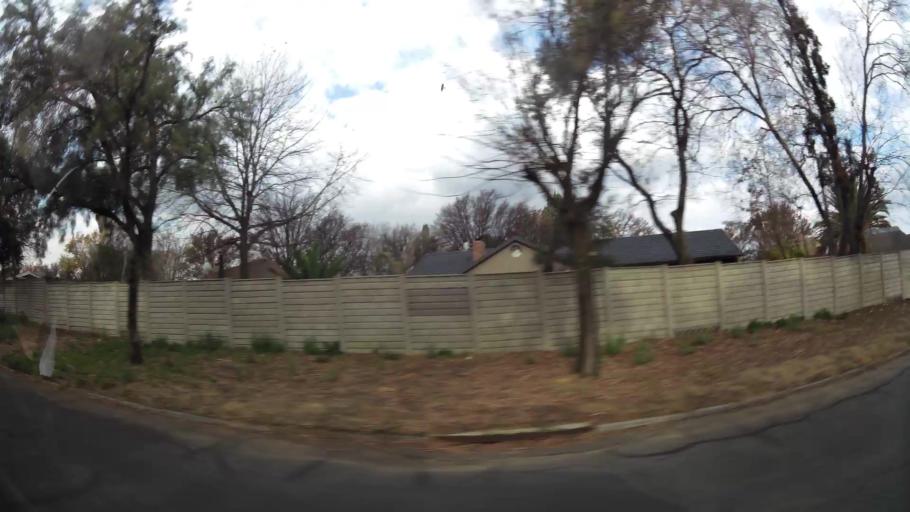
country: ZA
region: Orange Free State
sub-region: Fezile Dabi District Municipality
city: Sasolburg
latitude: -26.7921
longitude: 27.8157
